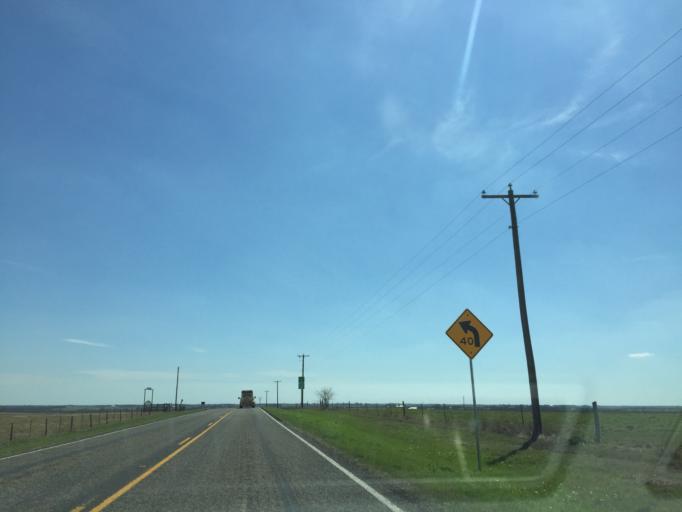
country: US
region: Texas
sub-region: Williamson County
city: Taylor
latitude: 30.5567
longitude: -97.3239
